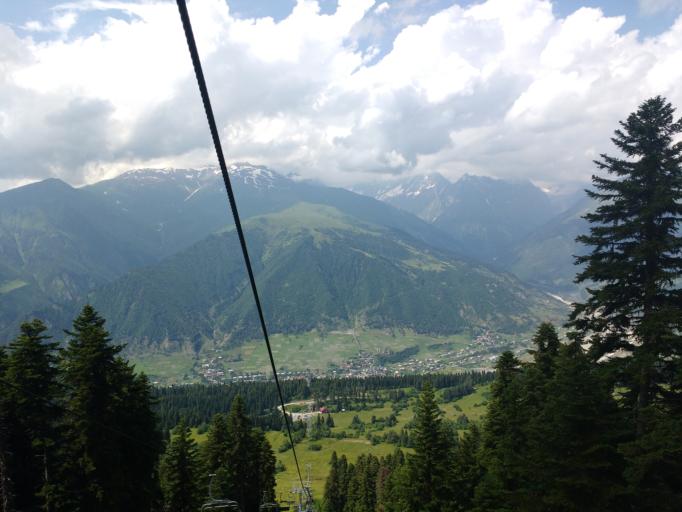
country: GE
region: Samegrelo and Zemo Svaneti
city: Mest'ia
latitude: 43.0199
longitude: 42.7379
